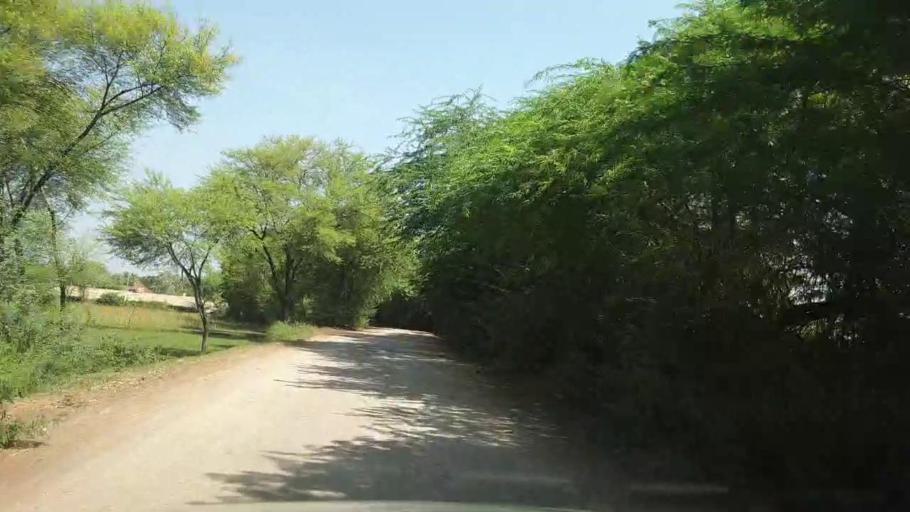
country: PK
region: Sindh
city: Rohri
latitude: 27.6906
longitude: 68.9492
